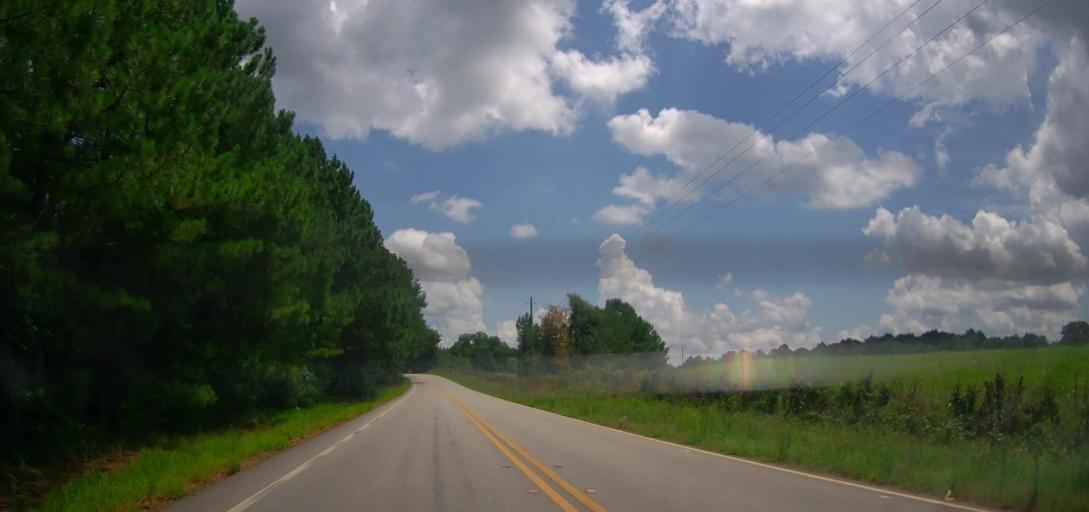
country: US
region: Georgia
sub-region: Meriwether County
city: Greenville
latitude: 33.0783
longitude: -84.7756
